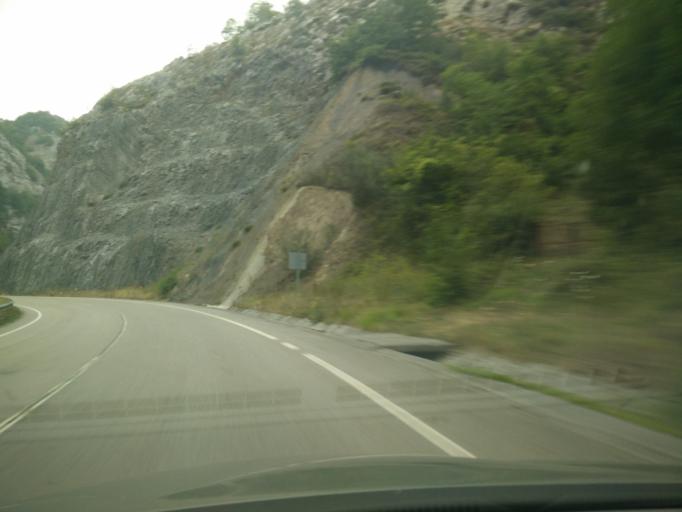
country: ES
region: Asturias
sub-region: Province of Asturias
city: Campo de Caso
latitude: 43.1815
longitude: -5.3635
